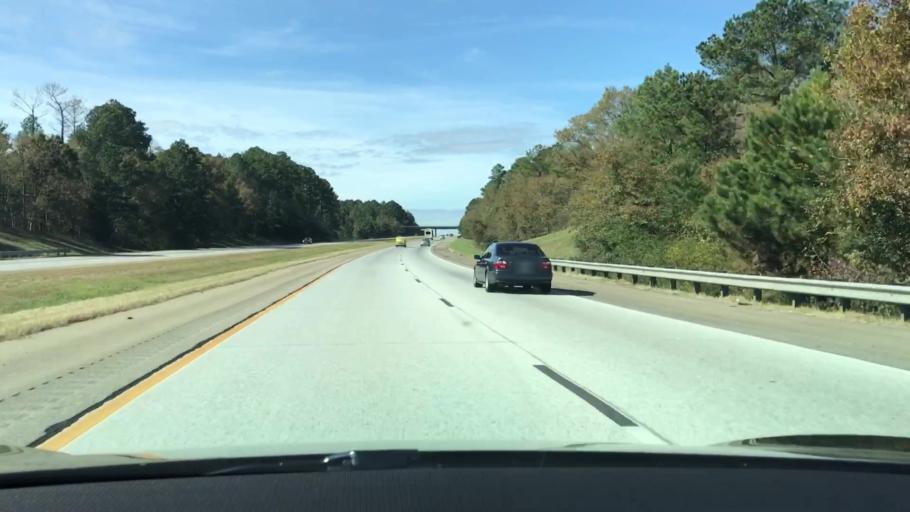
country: US
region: Georgia
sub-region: Greene County
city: Greensboro
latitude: 33.5363
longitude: -83.2446
